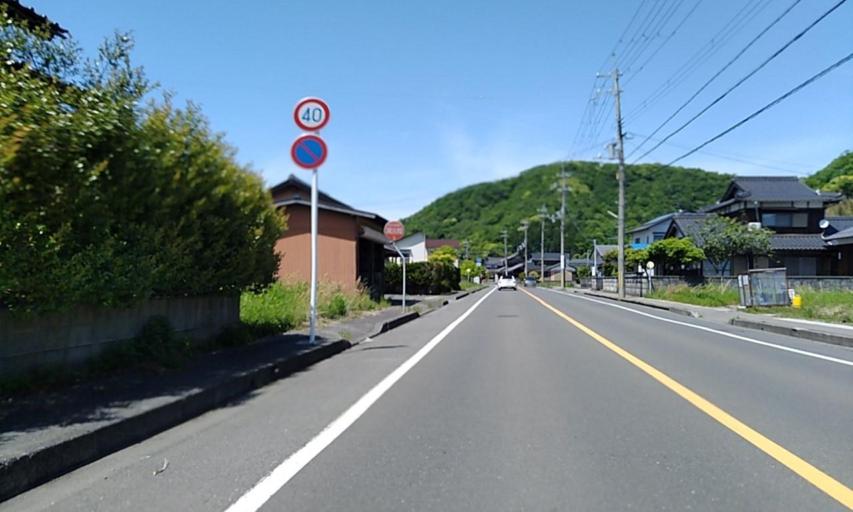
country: JP
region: Fukui
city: Obama
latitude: 35.5172
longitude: 135.7531
